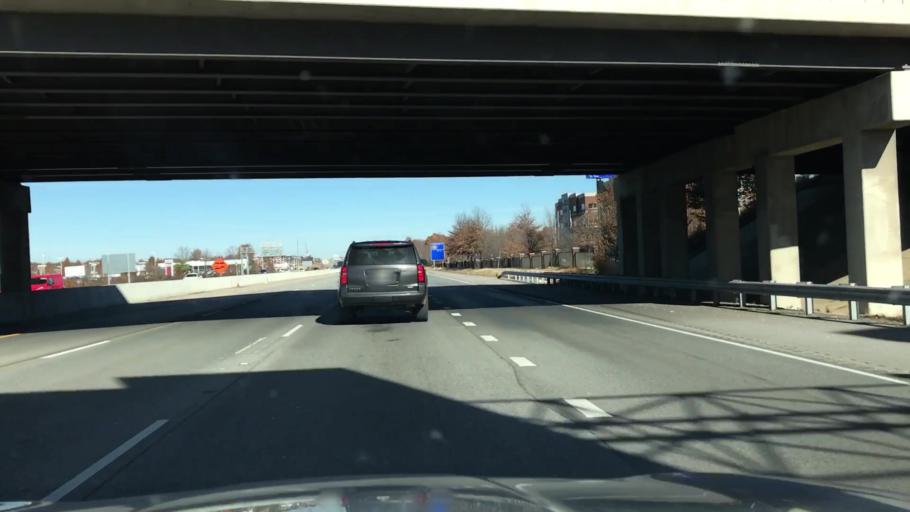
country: US
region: Arkansas
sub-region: Benton County
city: Bentonville
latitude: 36.3421
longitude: -94.1813
